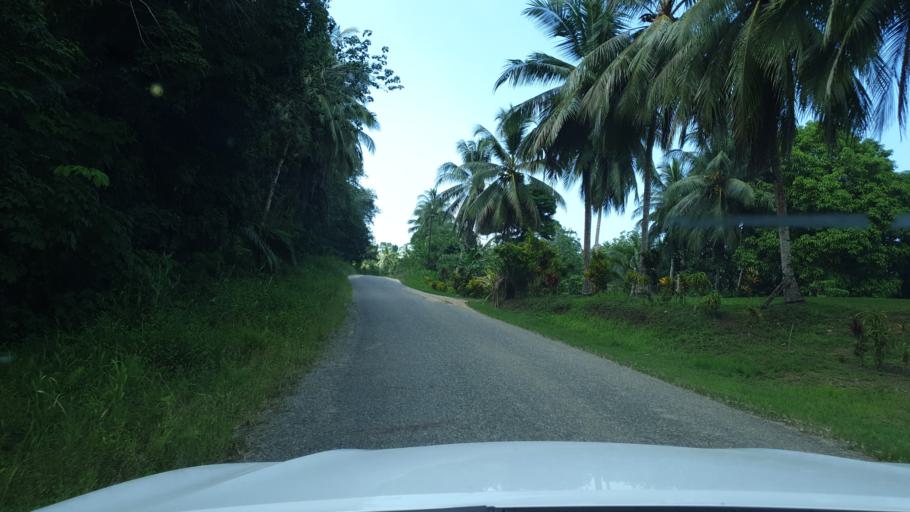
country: PG
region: East Sepik
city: Angoram
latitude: -3.9518
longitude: 144.0357
